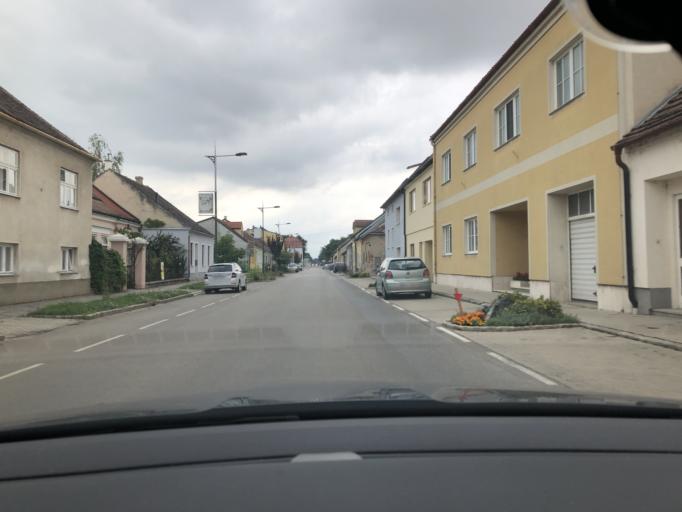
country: AT
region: Lower Austria
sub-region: Politischer Bezirk Mistelbach
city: Laa an der Thaya
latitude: 48.7273
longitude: 16.3837
